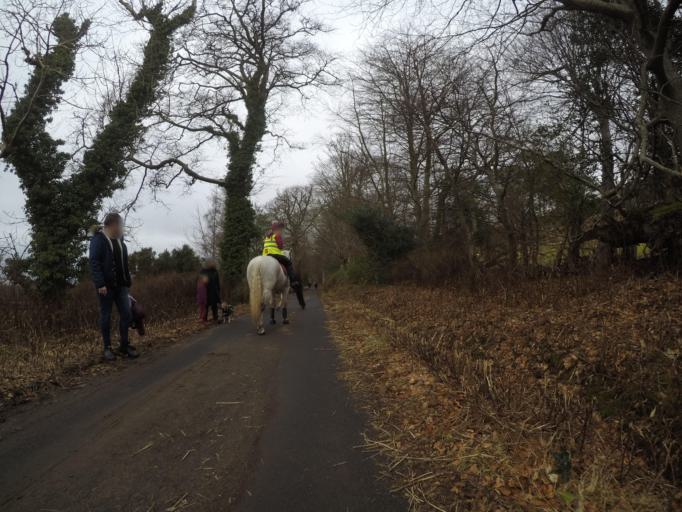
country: GB
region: Scotland
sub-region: North Ayrshire
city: Fairlie
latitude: 55.7632
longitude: -4.8475
